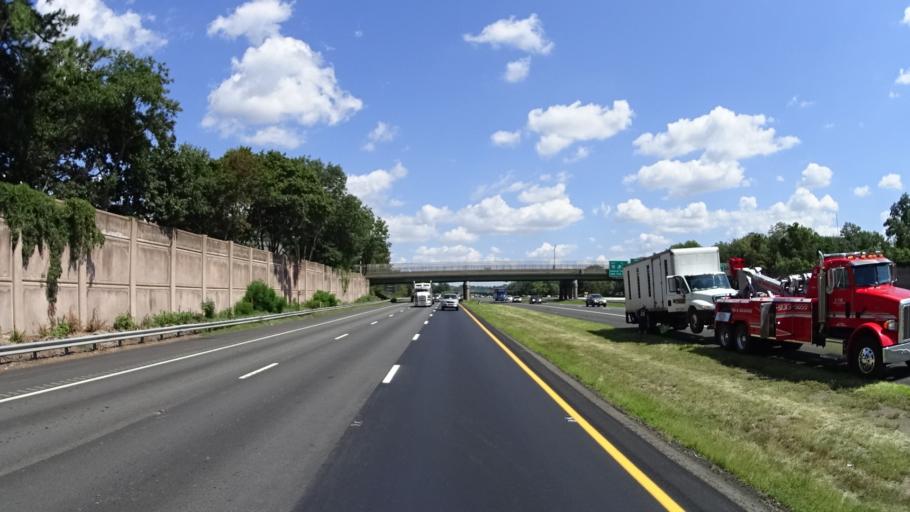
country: US
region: New Jersey
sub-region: Union County
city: Springfield
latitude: 40.7134
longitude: -74.3096
